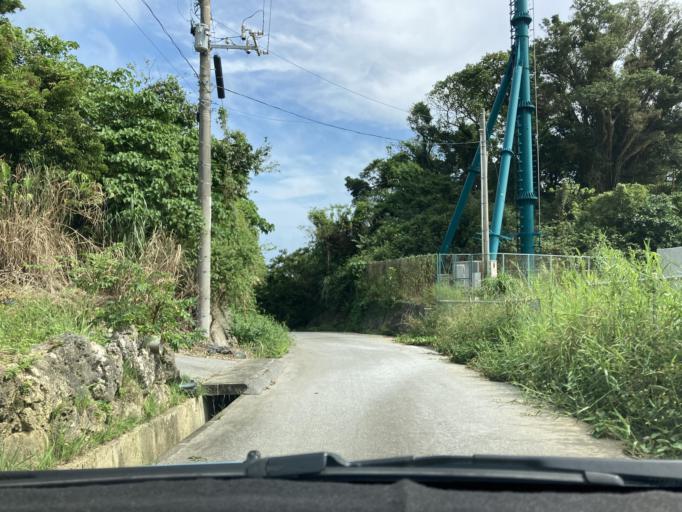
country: JP
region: Okinawa
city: Ginowan
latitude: 26.1598
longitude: 127.8113
